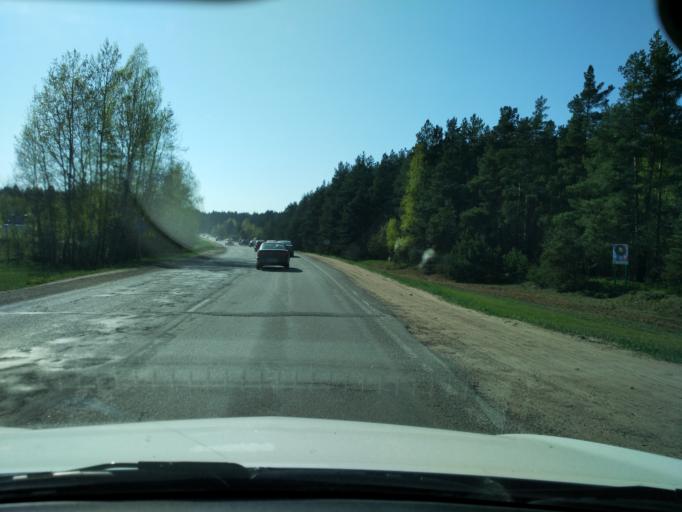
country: BY
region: Minsk
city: Lyeskawka
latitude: 53.9611
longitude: 27.7070
